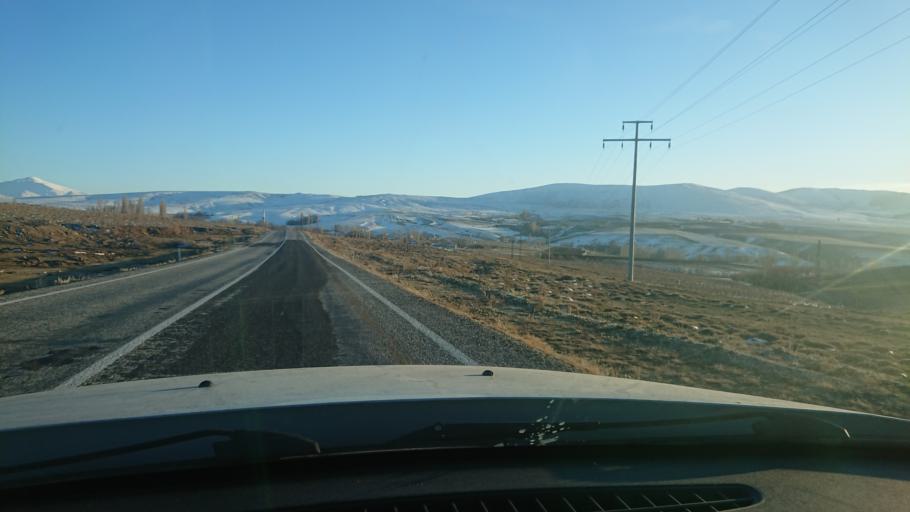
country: TR
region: Aksaray
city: Ortakoy
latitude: 38.7619
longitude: 33.9326
